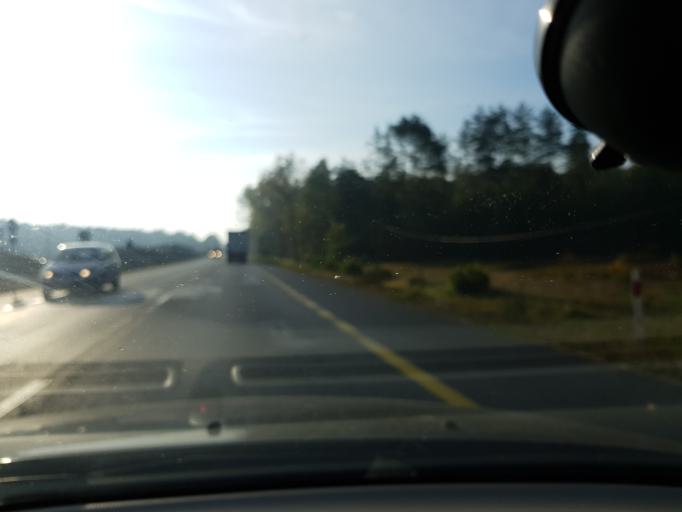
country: PL
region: Masovian Voivodeship
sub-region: Powiat otwocki
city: Otwock
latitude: 52.1506
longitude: 21.3171
